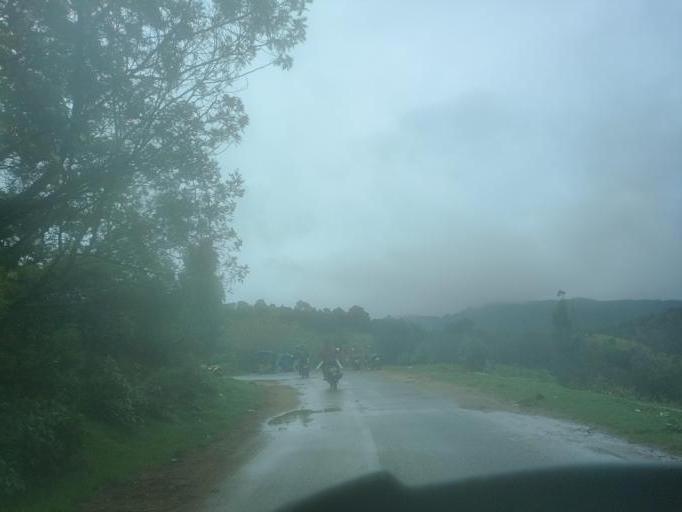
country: IN
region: Tamil Nadu
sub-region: Dindigul
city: Kodaikanal
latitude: 10.2234
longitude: 77.3551
